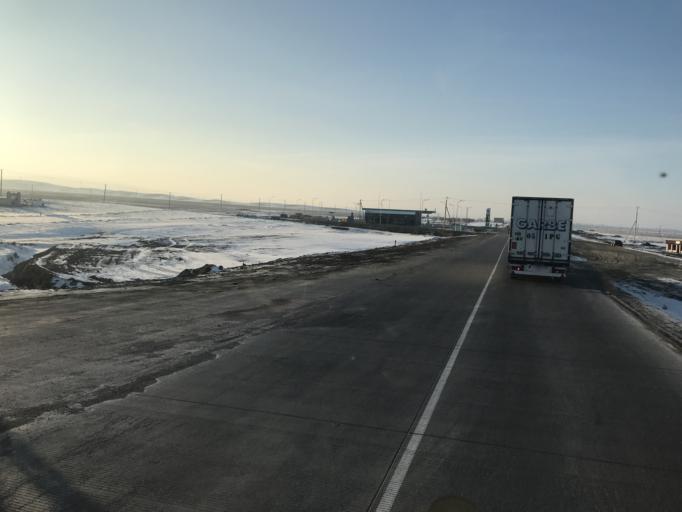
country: KG
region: Chuy
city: Ivanovka
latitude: 43.4003
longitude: 75.1143
